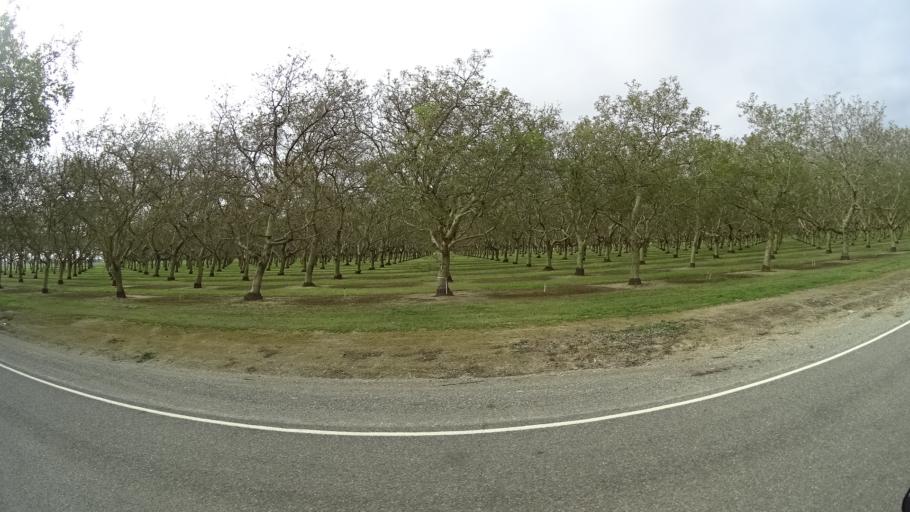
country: US
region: California
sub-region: Colusa County
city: Colusa
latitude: 39.4021
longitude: -121.9901
